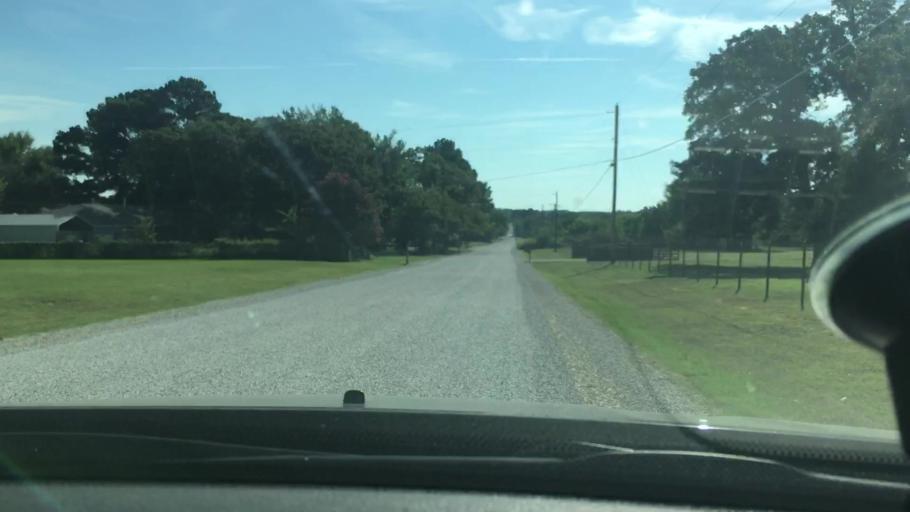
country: US
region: Oklahoma
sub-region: Carter County
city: Lone Grove
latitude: 34.2165
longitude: -97.2548
